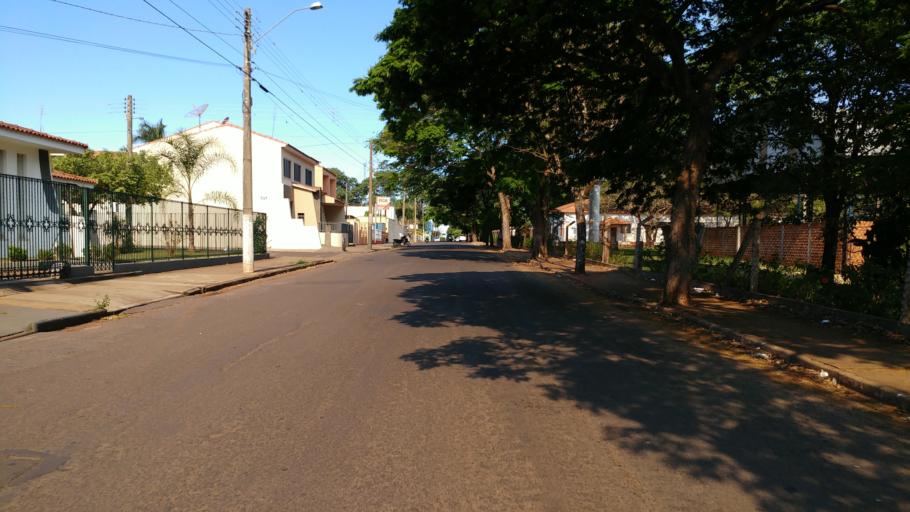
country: BR
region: Sao Paulo
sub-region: Paraguacu Paulista
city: Paraguacu Paulista
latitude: -22.4149
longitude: -50.5833
